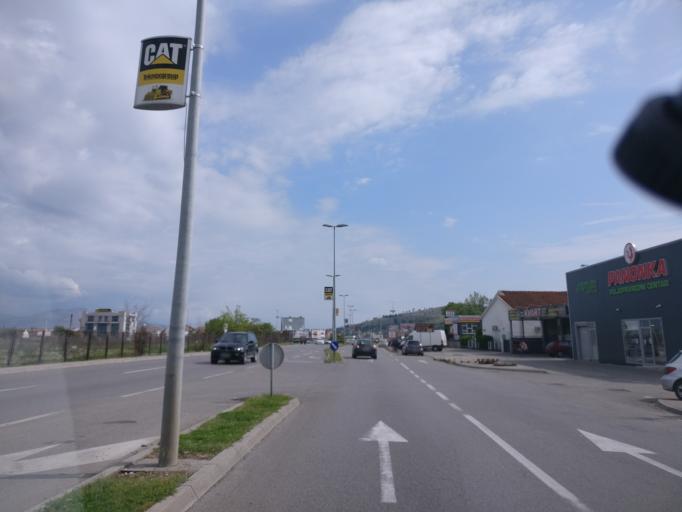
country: ME
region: Podgorica
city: Podgorica
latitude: 42.4366
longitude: 19.2272
